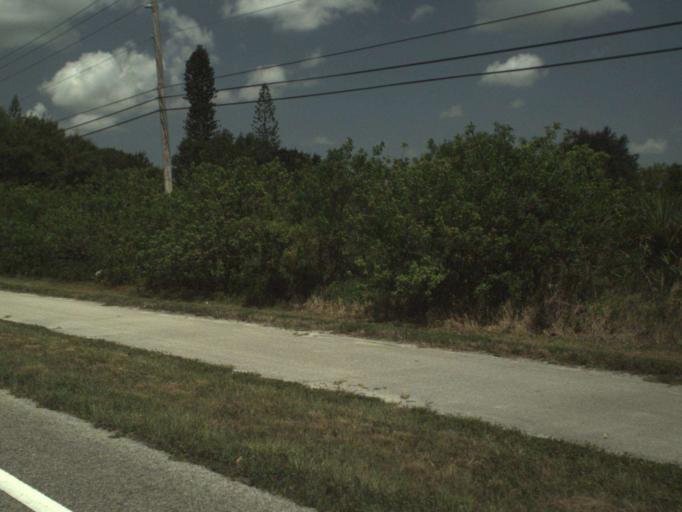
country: US
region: Florida
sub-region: Saint Lucie County
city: Fort Pierce South
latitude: 27.4040
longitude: -80.4391
